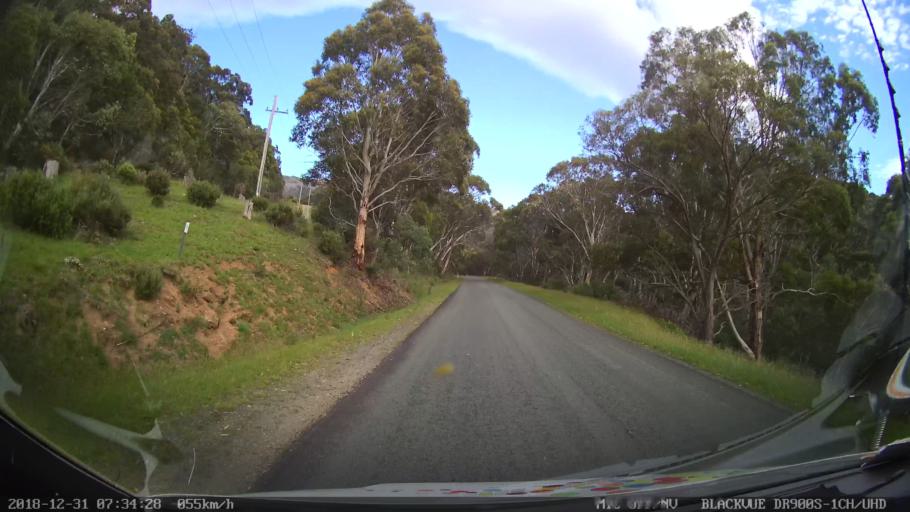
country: AU
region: New South Wales
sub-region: Snowy River
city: Jindabyne
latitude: -36.3335
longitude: 148.4518
